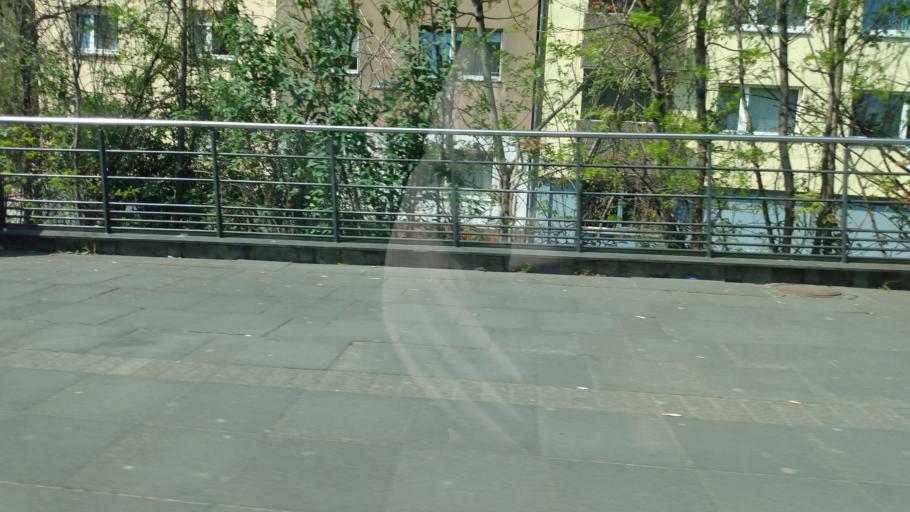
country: DE
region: North Rhine-Westphalia
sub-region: Regierungsbezirk Koln
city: Muelheim
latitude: 50.9612
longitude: 7.0034
